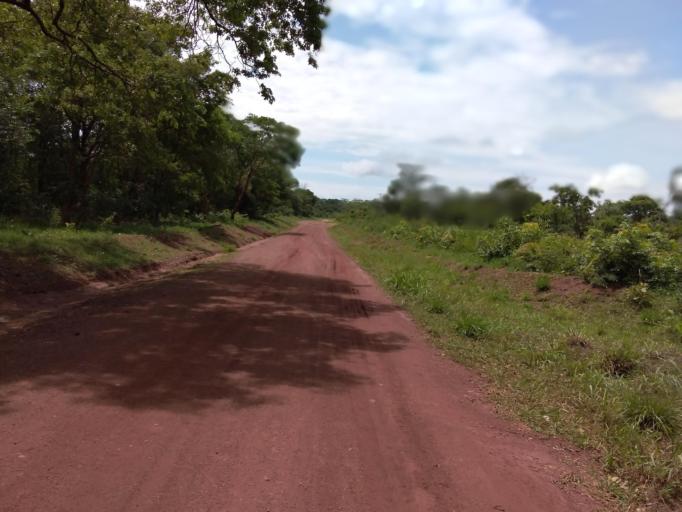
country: ZM
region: Copperbelt
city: Luanshya
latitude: -13.4819
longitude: 28.7725
